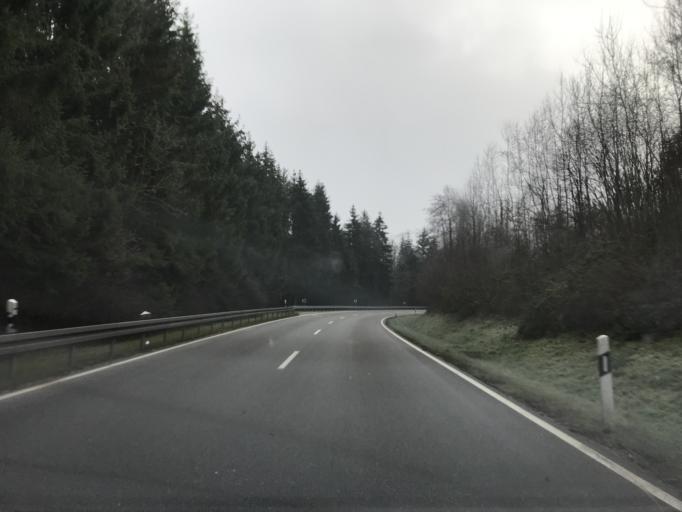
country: DE
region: Baden-Wuerttemberg
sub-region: Freiburg Region
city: Hasel
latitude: 47.6435
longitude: 7.8923
